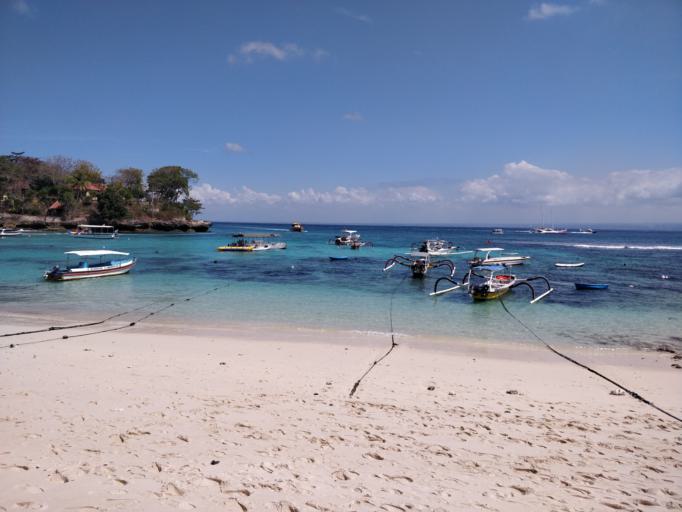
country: ID
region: Bali
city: Lembongan Kawan
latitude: -8.6822
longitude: 115.4337
